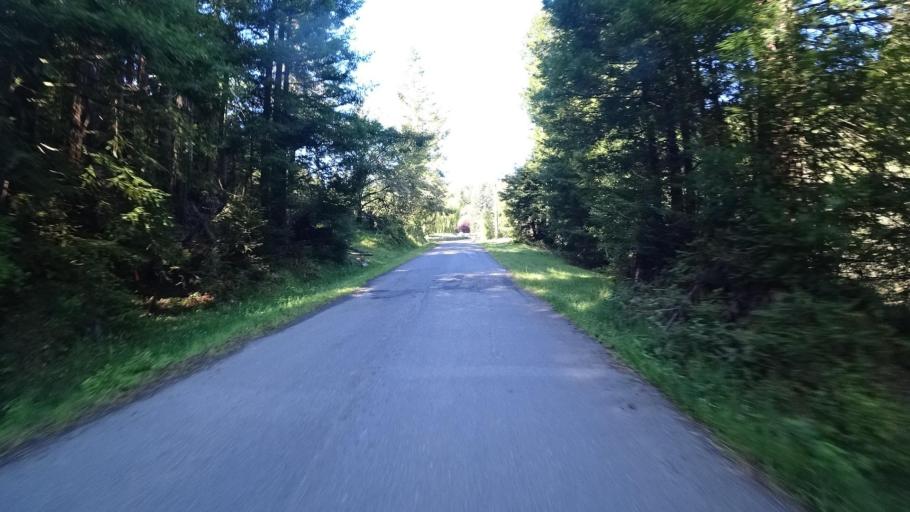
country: US
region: California
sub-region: Humboldt County
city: Fortuna
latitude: 40.5270
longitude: -124.1863
